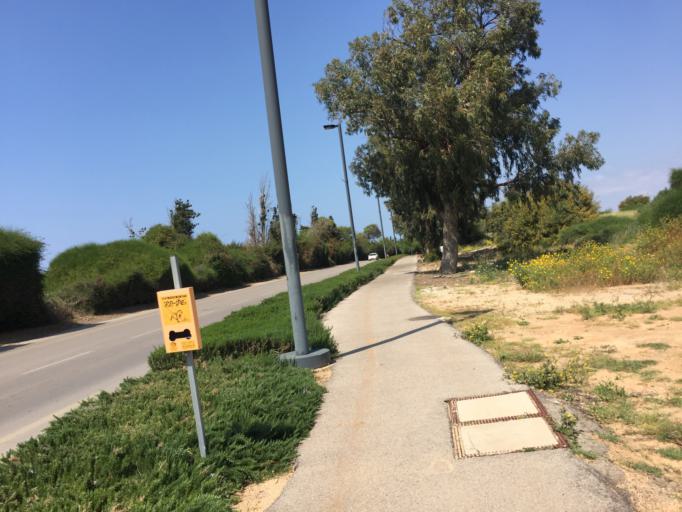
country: IL
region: Haifa
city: Qesarya
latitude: 32.4990
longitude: 34.9039
